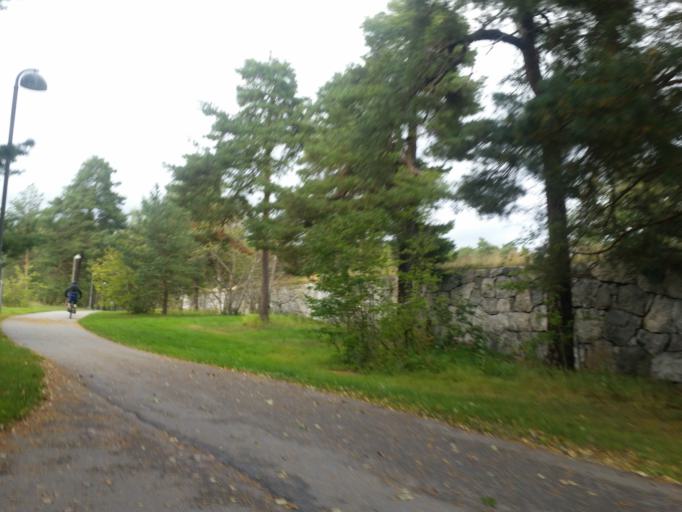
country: SE
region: Stockholm
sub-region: Stockholms Kommun
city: Arsta
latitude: 59.2760
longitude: 18.0952
